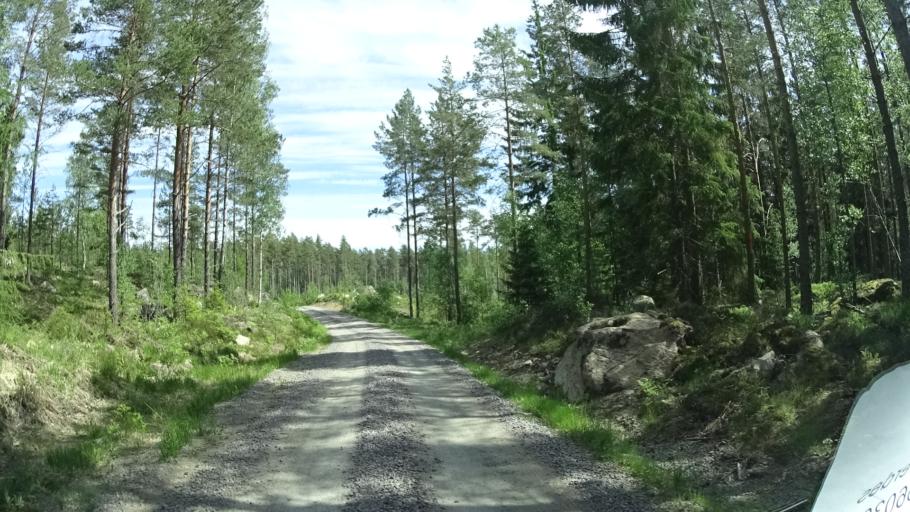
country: SE
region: OEstergoetland
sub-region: Norrkopings Kommun
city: Svartinge
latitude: 58.7707
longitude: 15.9617
